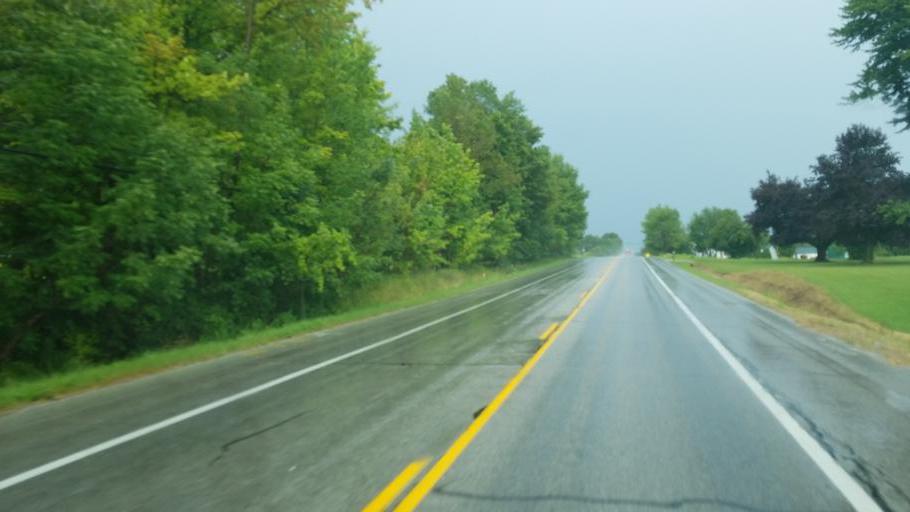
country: US
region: Ohio
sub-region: Geauga County
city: Middlefield
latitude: 41.4585
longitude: -80.9696
